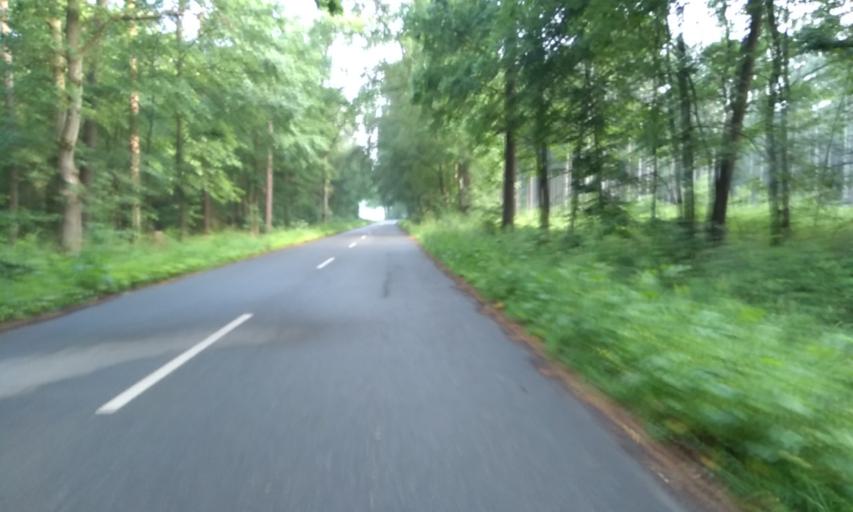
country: DE
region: Lower Saxony
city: Bargstedt
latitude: 53.5016
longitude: 9.4548
